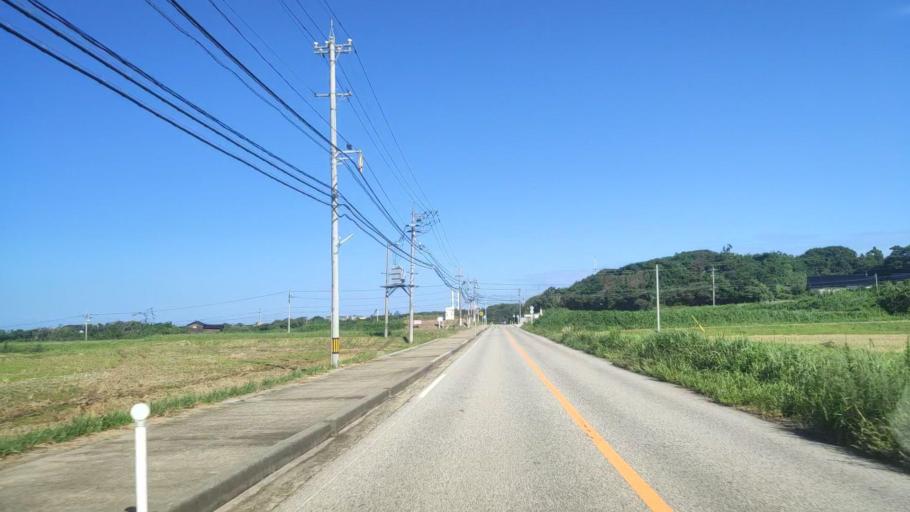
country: JP
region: Ishikawa
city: Hakui
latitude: 37.0468
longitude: 136.7377
